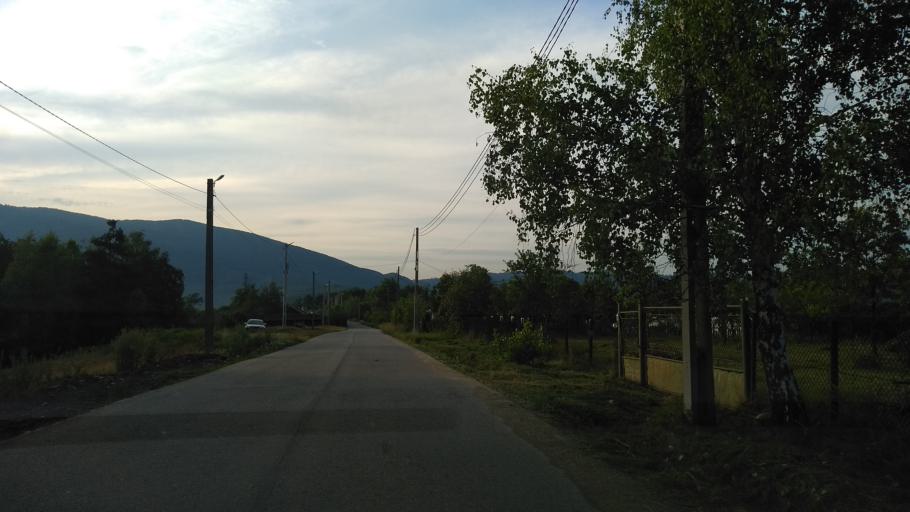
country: RO
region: Hunedoara
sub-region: Municipiul  Vulcan
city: Jiu-Paroseni
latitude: 45.3573
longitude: 23.2887
